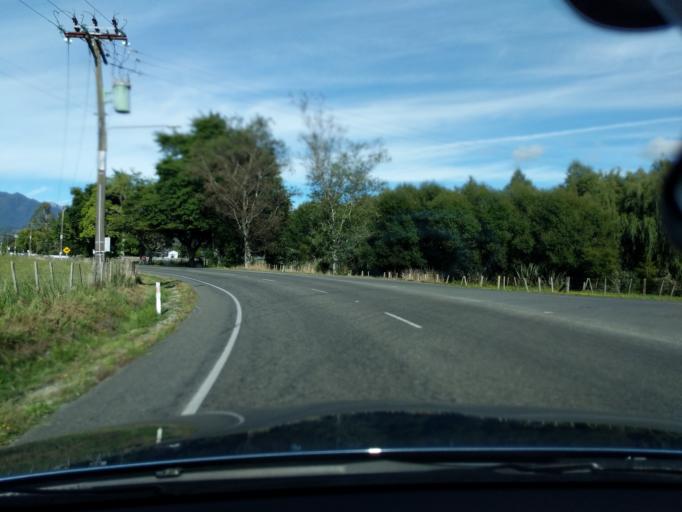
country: NZ
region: Tasman
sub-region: Tasman District
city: Takaka
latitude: -40.8554
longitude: 172.8145
